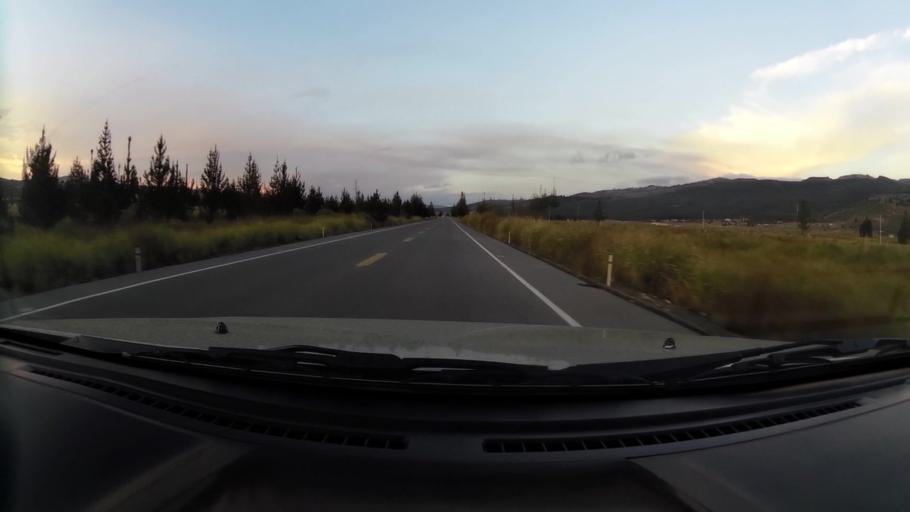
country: EC
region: Chimborazo
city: Alausi
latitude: -2.0226
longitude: -78.7325
